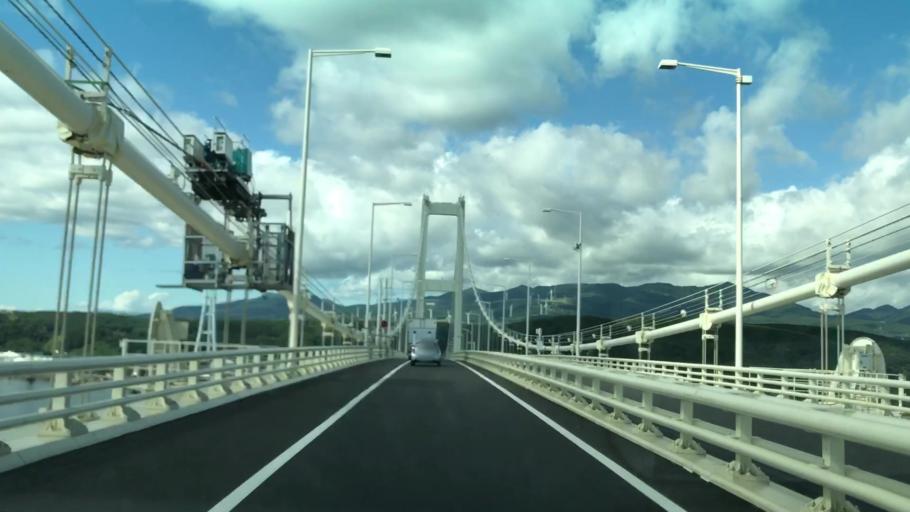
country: JP
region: Hokkaido
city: Muroran
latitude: 42.3522
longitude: 140.9500
